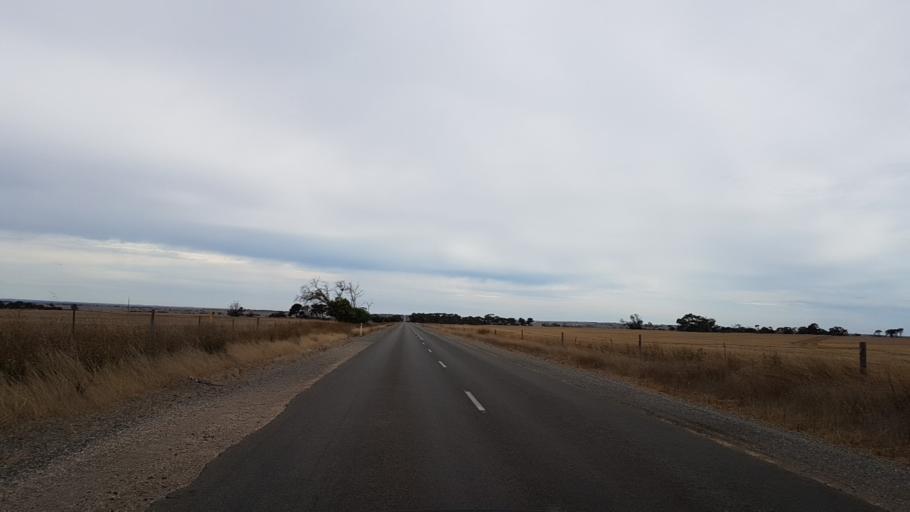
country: AU
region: South Australia
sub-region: Yorke Peninsula
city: Honiton
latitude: -34.9850
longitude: 137.3009
